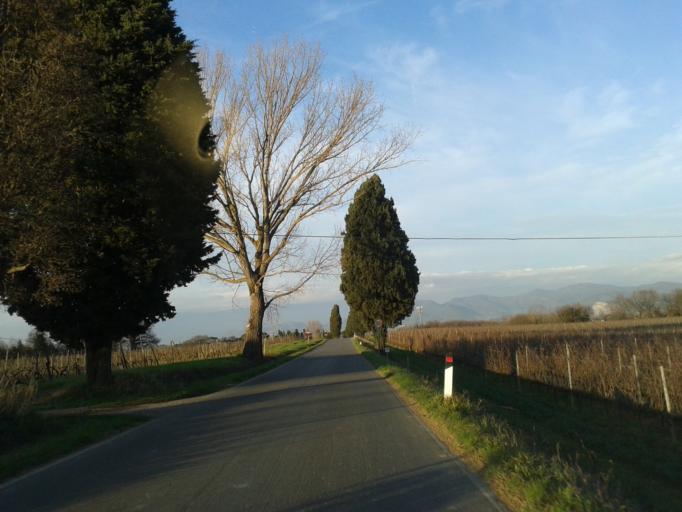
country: IT
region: Tuscany
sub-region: Provincia di Livorno
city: Vicarello
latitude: 43.5901
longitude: 10.4456
